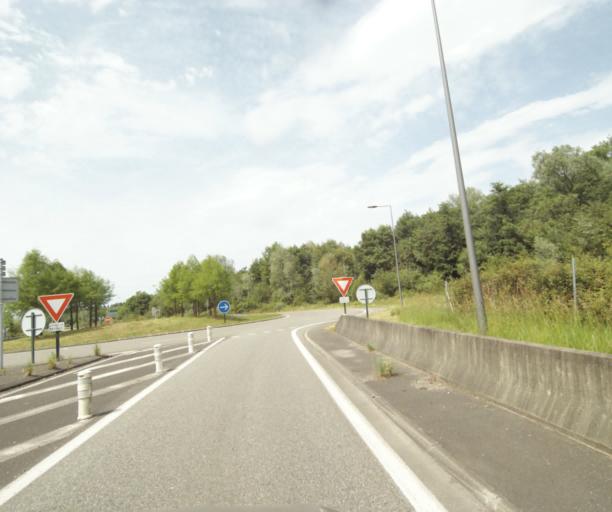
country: FR
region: Aquitaine
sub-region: Departement des Pyrenees-Atlantiques
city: Mouguerre
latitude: 43.4789
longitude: -1.4389
